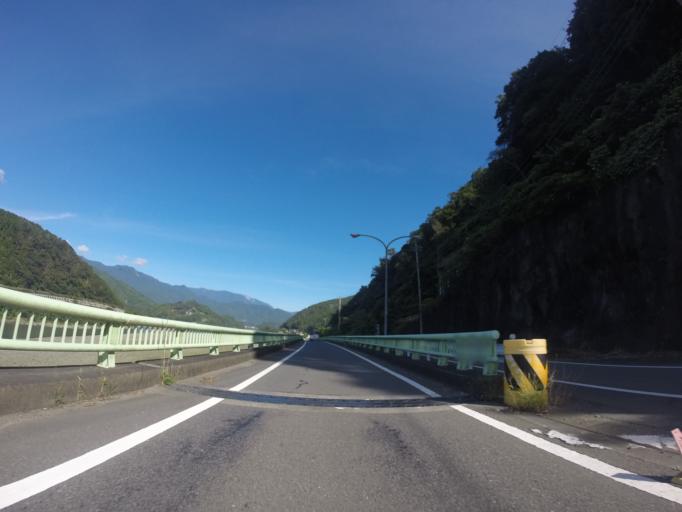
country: JP
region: Shizuoka
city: Fujinomiya
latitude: 35.2564
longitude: 138.4812
